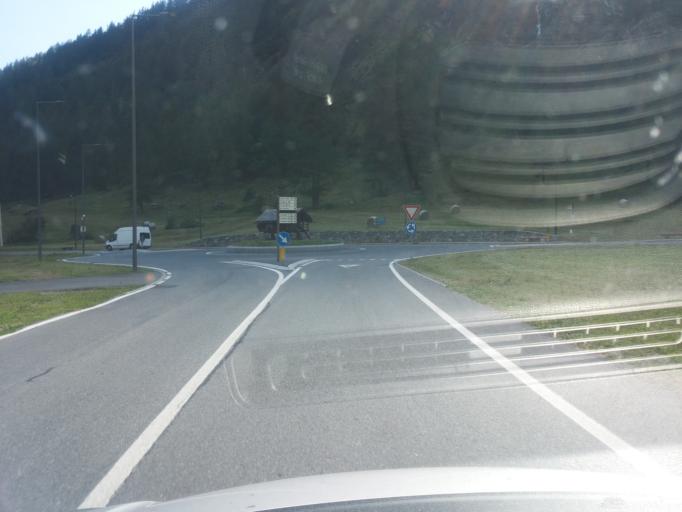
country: IT
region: Aosta Valley
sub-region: Valle d'Aosta
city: Gressoney-La-Trinite
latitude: 45.8242
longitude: 7.8239
